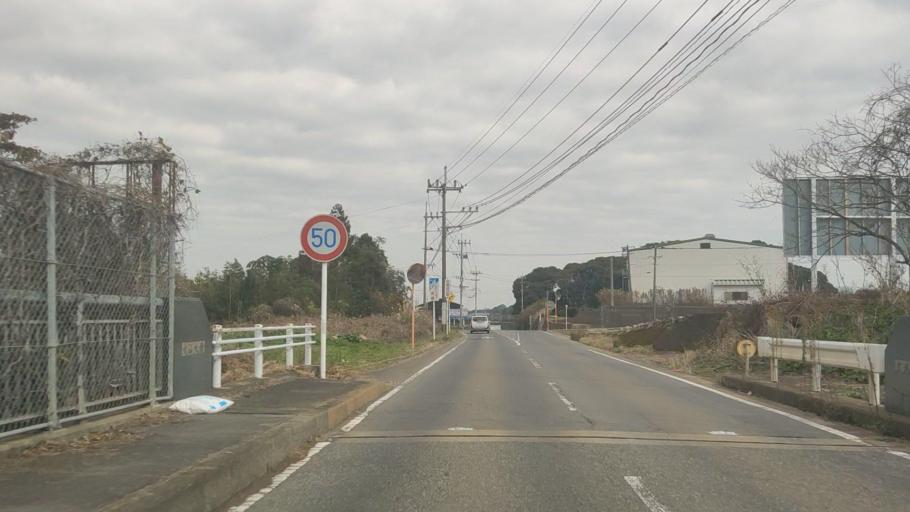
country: JP
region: Nagasaki
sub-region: Isahaya-shi
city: Isahaya
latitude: 32.8083
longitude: 130.1698
